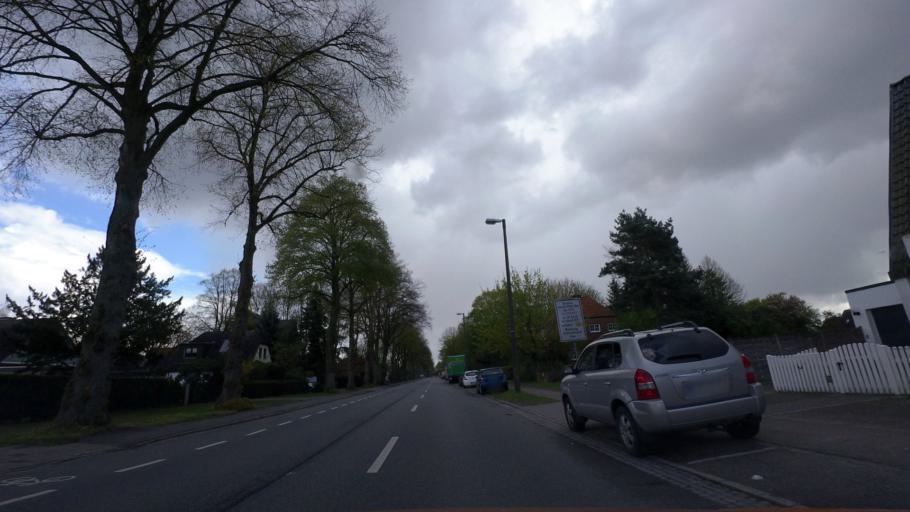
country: DE
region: Lower Saxony
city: Stuhr
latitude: 53.0562
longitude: 8.7114
